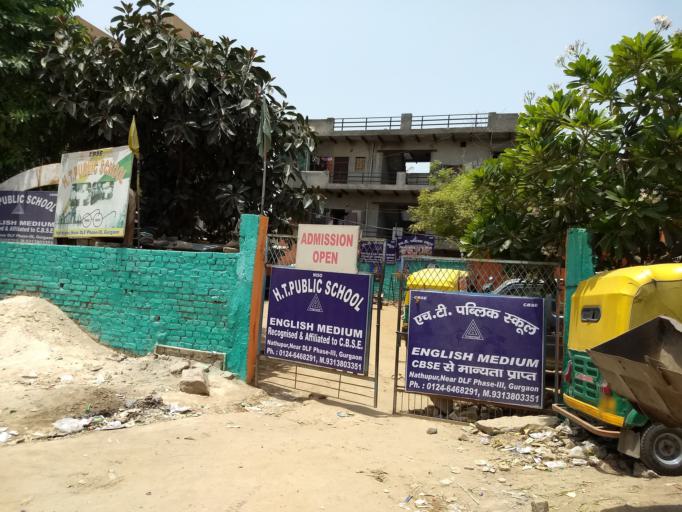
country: IN
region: Haryana
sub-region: Gurgaon
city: Gurgaon
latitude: 28.4905
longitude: 77.0972
